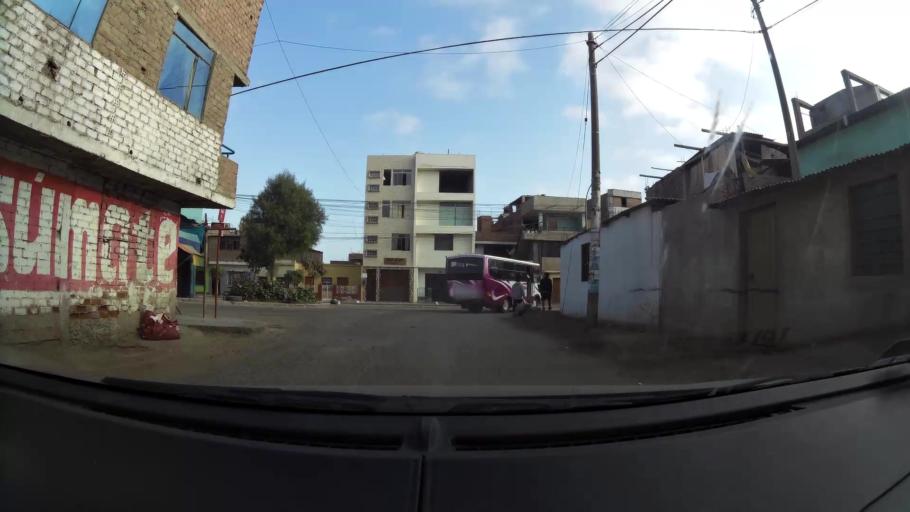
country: PE
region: La Libertad
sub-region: Provincia de Trujillo
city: El Porvenir
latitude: -8.0861
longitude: -79.0104
